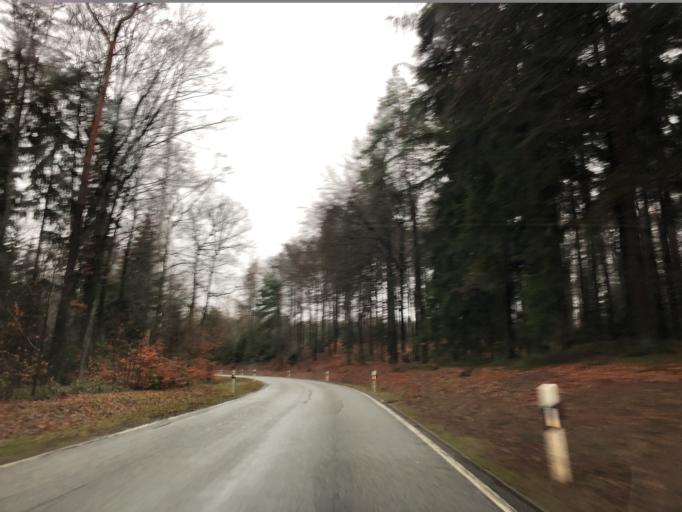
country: DE
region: Hesse
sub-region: Regierungsbezirk Darmstadt
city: Lutzelbach
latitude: 49.7508
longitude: 9.0819
